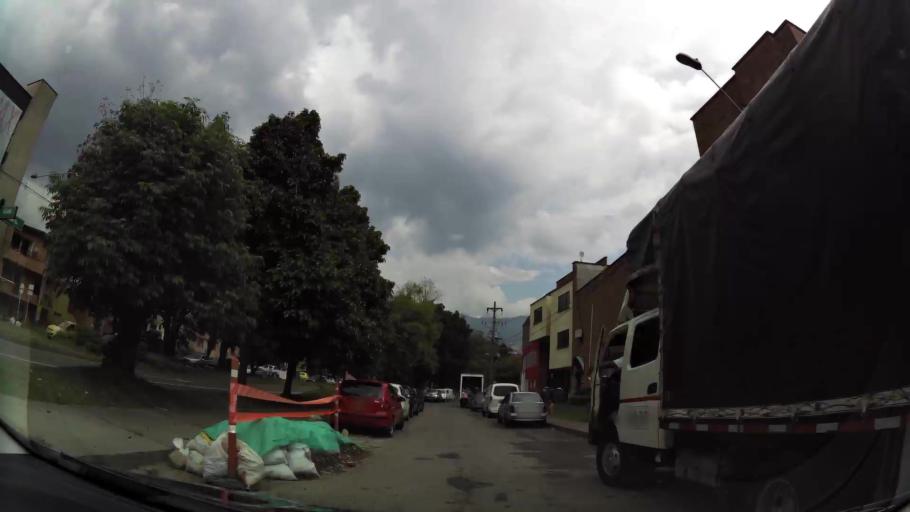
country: CO
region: Antioquia
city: Itagui
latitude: 6.2030
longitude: -75.5851
